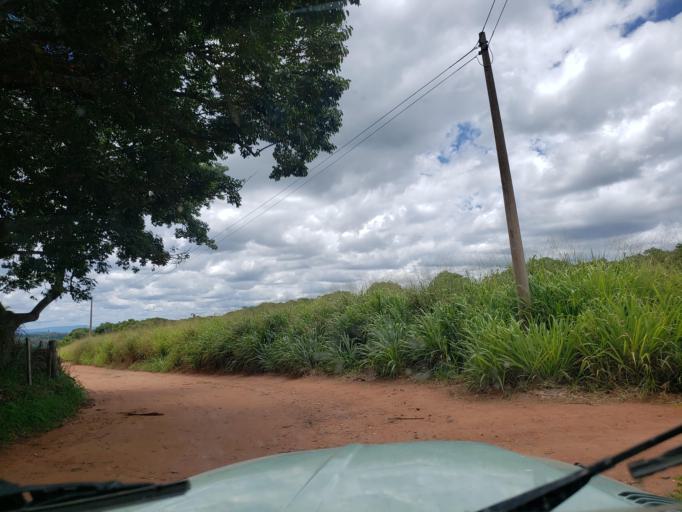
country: BR
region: Sao Paulo
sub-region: Santo Antonio Do Jardim
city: Espirito Santo do Pinhal
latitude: -22.2173
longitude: -46.8369
